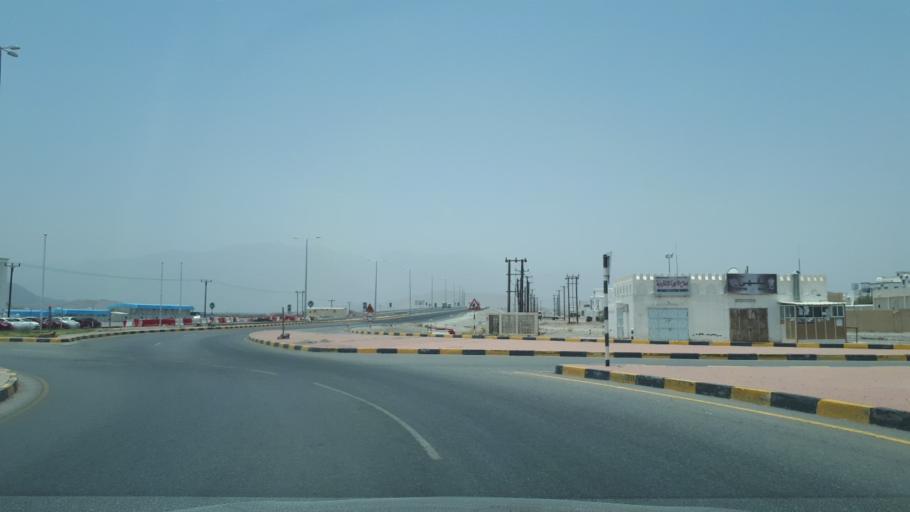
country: OM
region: Al Batinah
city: Rustaq
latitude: 23.4724
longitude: 57.4457
